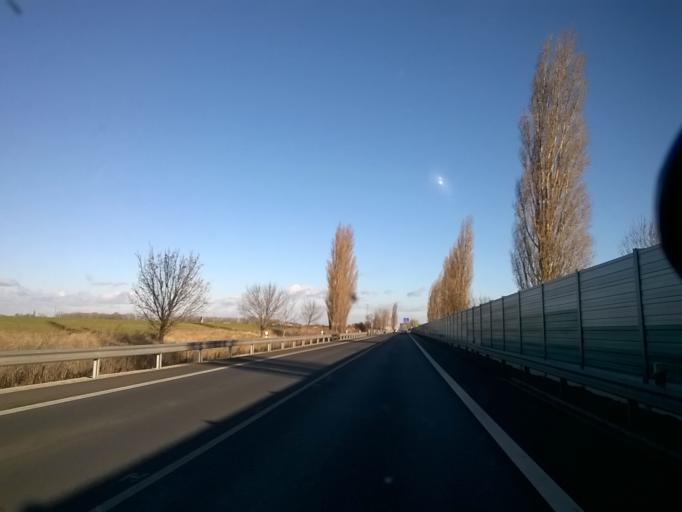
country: SK
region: Trnavsky
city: Sladkovicovo
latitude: 48.2044
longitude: 17.6239
